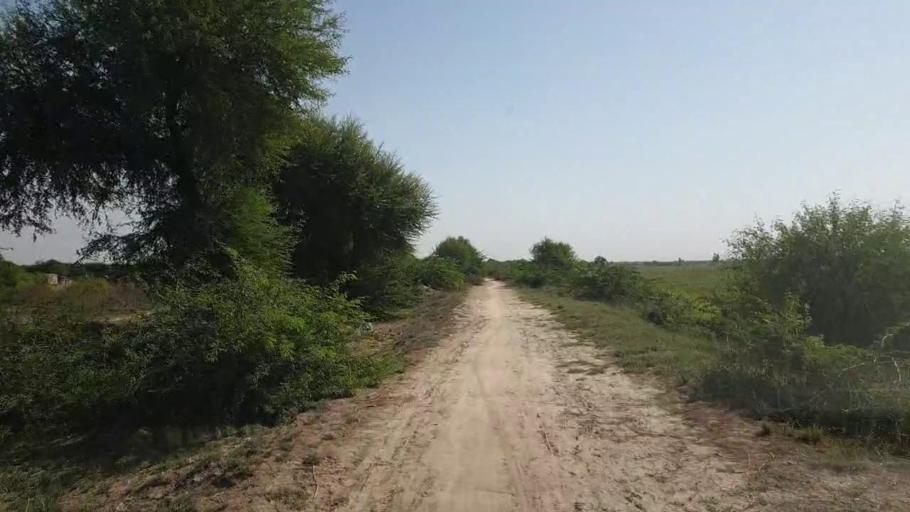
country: PK
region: Sindh
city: Kadhan
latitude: 24.6071
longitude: 69.0013
